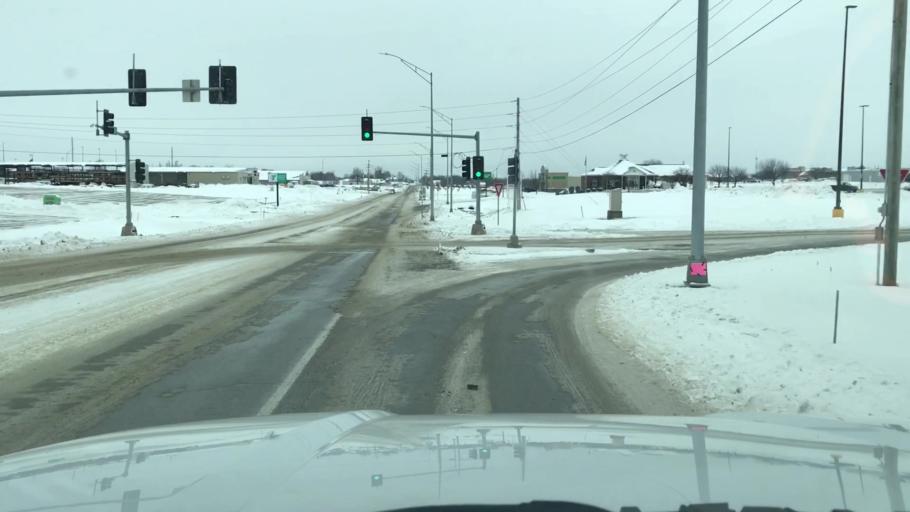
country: US
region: Missouri
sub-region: Clinton County
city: Cameron
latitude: 39.7577
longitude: -94.2343
